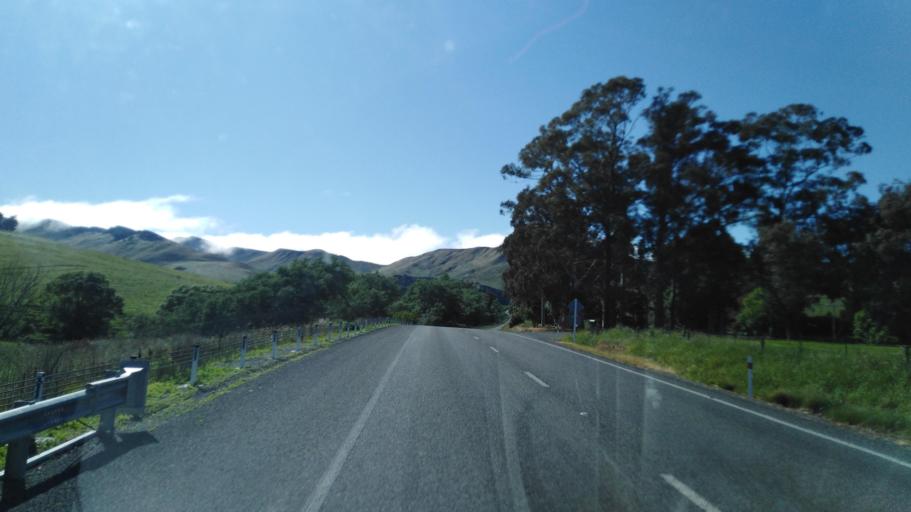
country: NZ
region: Canterbury
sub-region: Hurunui District
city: Amberley
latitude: -42.9777
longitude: 172.7089
